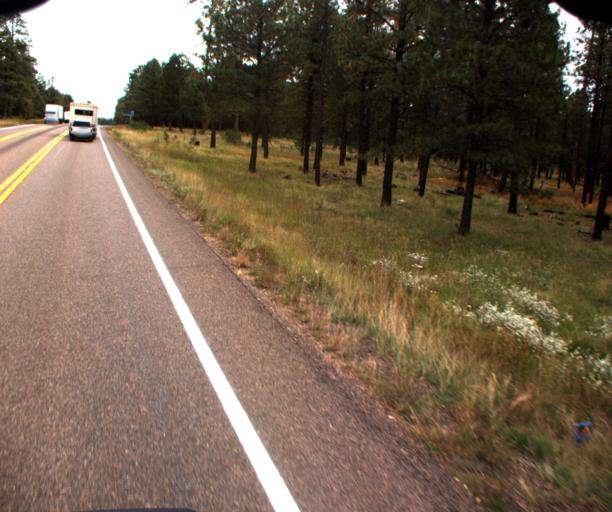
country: US
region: Arizona
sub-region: Navajo County
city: Heber-Overgaard
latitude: 34.3308
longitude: -110.7881
